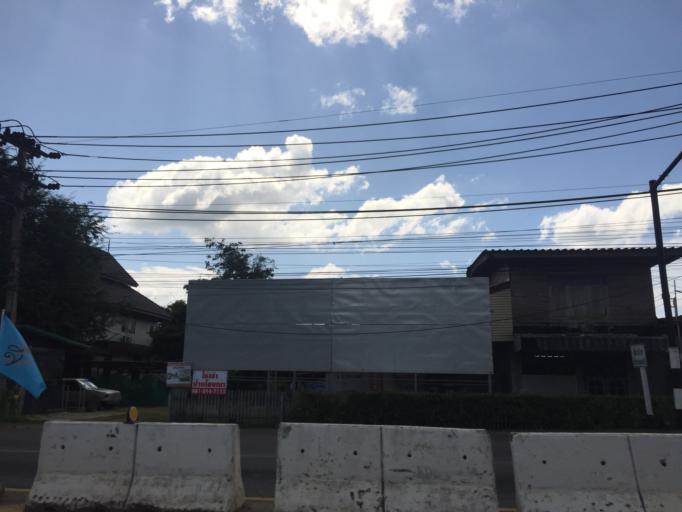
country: TH
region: Phangnga
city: Ban Ao Nang
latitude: 8.0732
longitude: 98.8381
